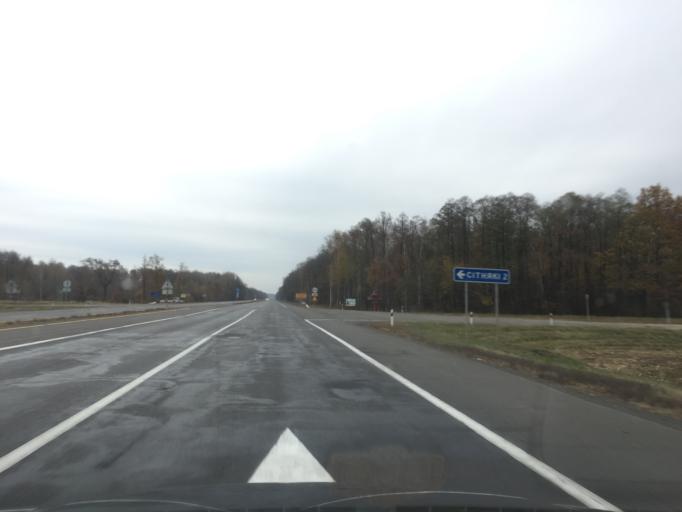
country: BY
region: Gomel
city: Horad Rechytsa
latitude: 52.3474
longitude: 30.5777
